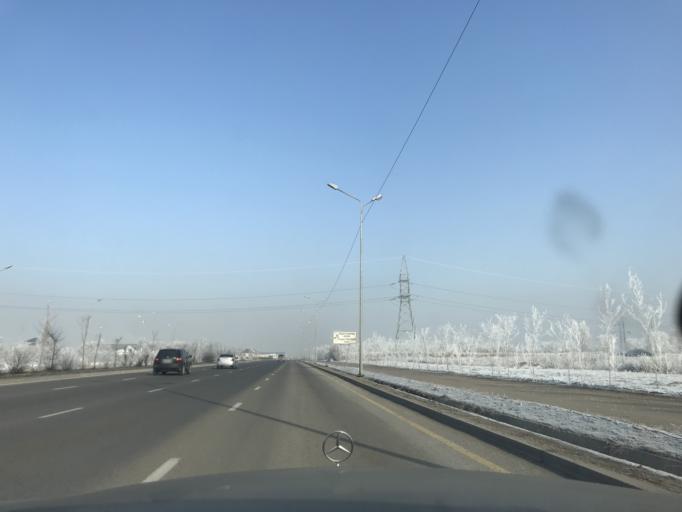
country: KZ
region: Almaty Oblysy
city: Burunday
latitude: 43.3326
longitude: 76.8335
